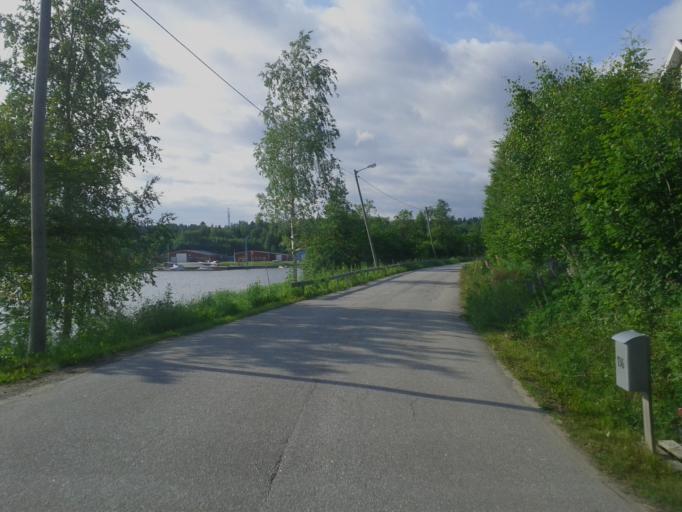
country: SE
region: Vaesternorrland
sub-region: OErnskoeldsviks Kommun
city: Ornskoldsvik
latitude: 63.2666
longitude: 18.8067
